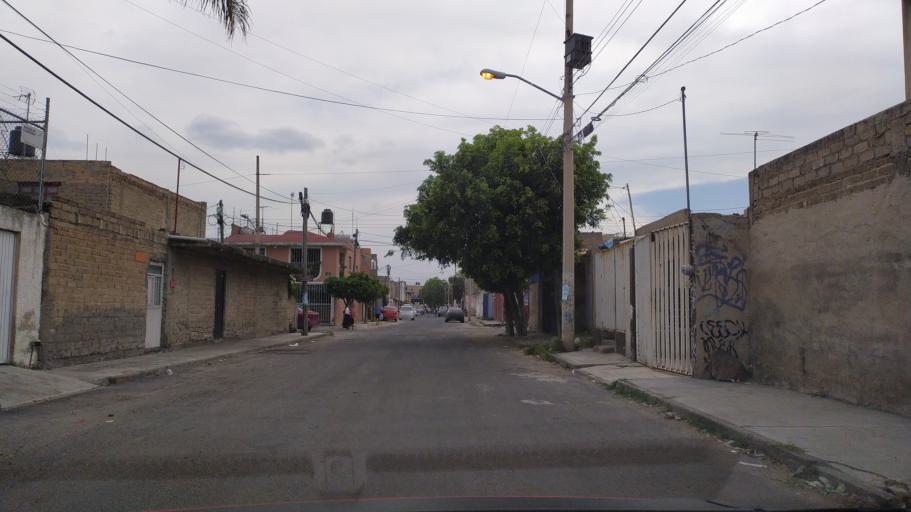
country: MX
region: Jalisco
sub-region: Tlajomulco de Zuniga
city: Palomar
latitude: 20.6467
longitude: -103.4507
